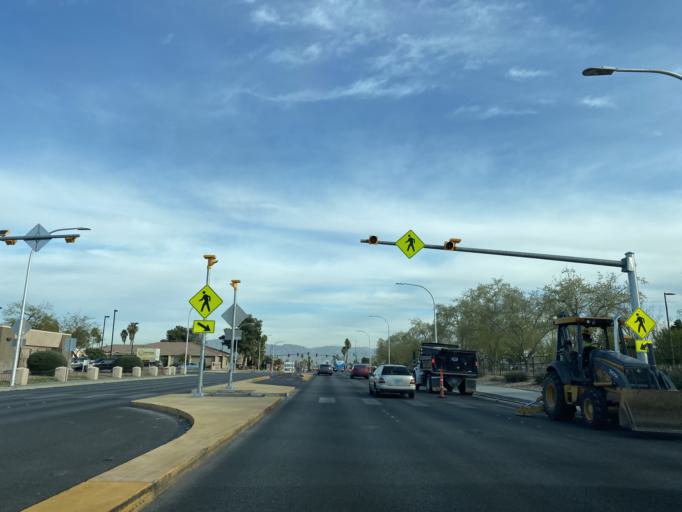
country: US
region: Nevada
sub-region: Clark County
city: Winchester
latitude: 36.1461
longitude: -115.1187
